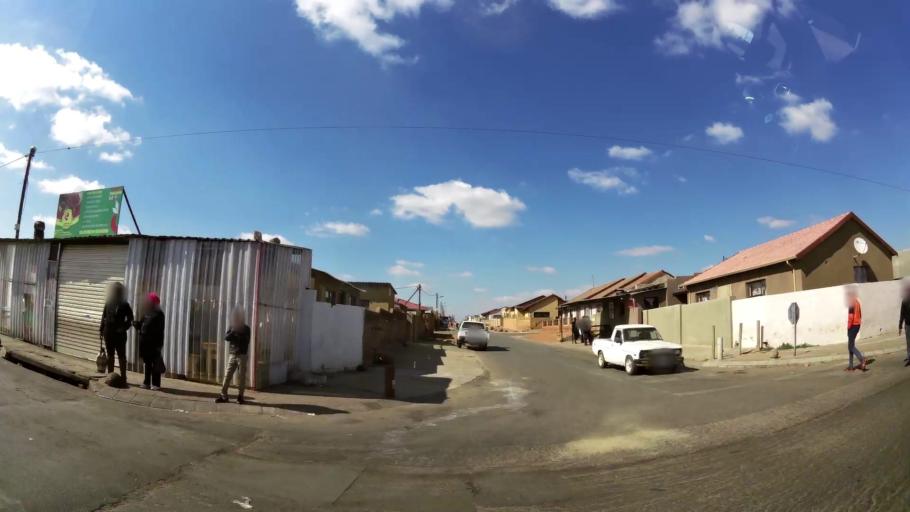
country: ZA
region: Gauteng
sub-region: West Rand District Municipality
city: Krugersdorp
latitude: -26.1549
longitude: 27.7853
